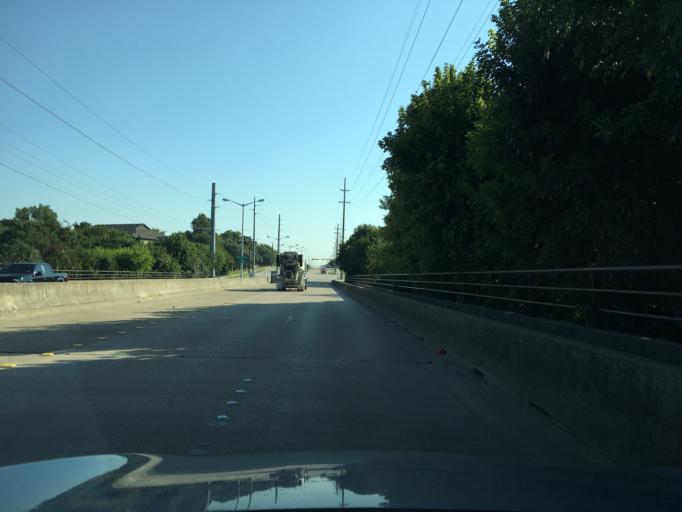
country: US
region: Texas
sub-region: Dallas County
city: Garland
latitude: 32.9589
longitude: -96.6502
